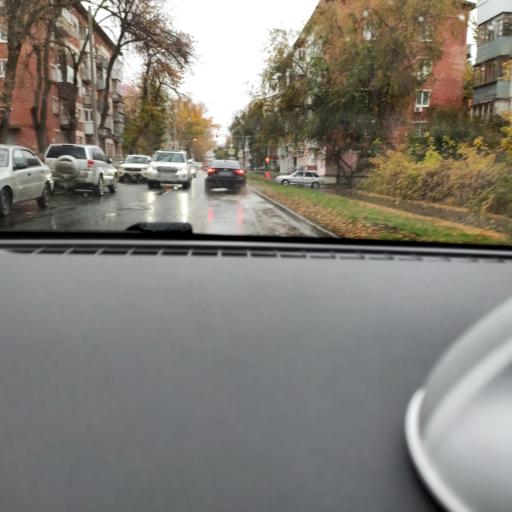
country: RU
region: Samara
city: Samara
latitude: 53.2136
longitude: 50.1550
